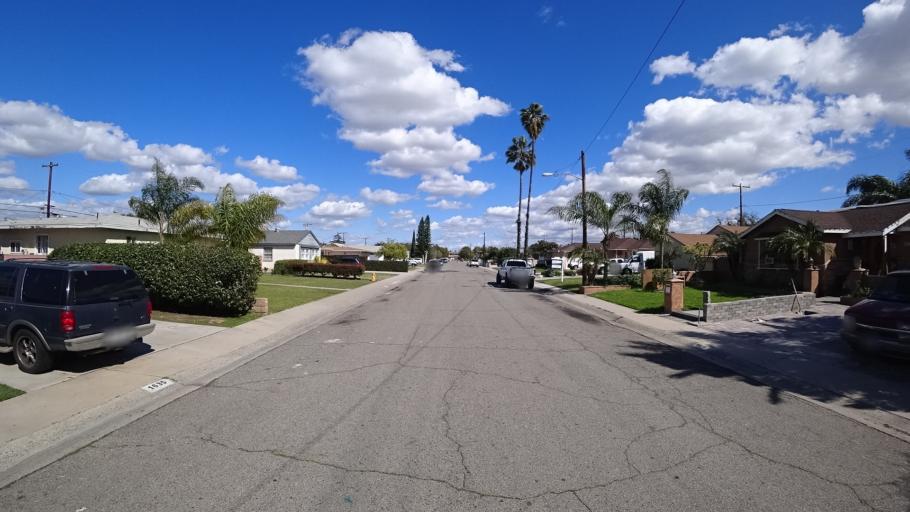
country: US
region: California
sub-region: Orange County
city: Anaheim
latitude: 33.8369
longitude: -117.8938
